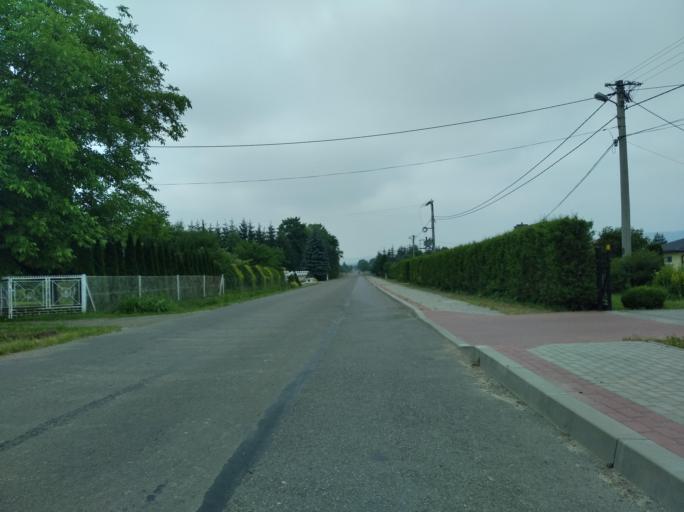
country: PL
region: Subcarpathian Voivodeship
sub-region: Powiat krosnienski
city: Sieniawa
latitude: 49.5751
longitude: 21.9235
